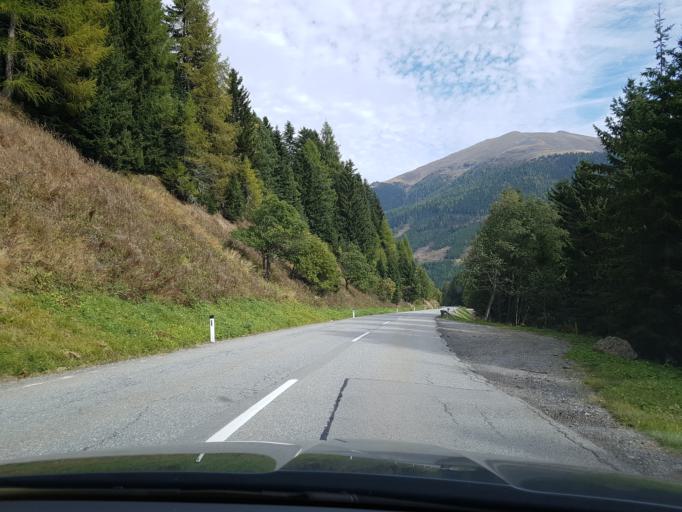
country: AT
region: Salzburg
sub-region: Politischer Bezirk Tamsweg
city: Ramingstein
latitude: 46.9356
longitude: 13.8765
